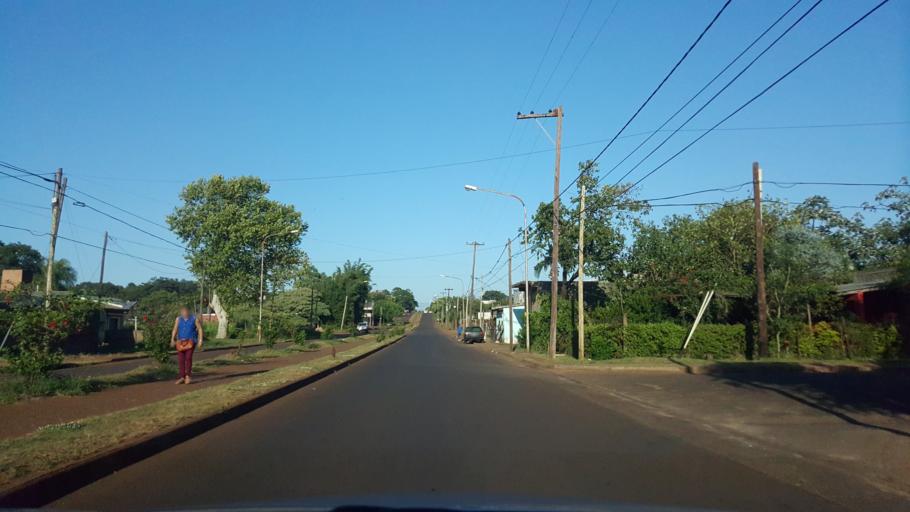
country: AR
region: Misiones
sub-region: Departamento de Capital
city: Posadas
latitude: -27.3986
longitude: -55.9235
